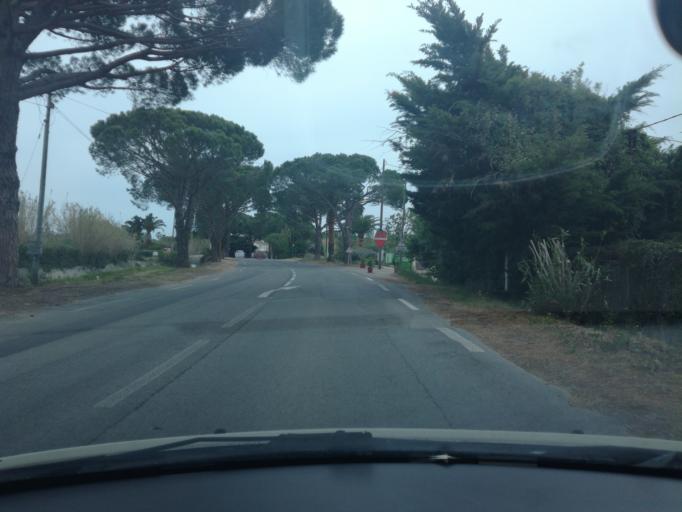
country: FR
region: Provence-Alpes-Cote d'Azur
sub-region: Departement du Var
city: Hyeres
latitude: 43.1110
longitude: 6.1678
